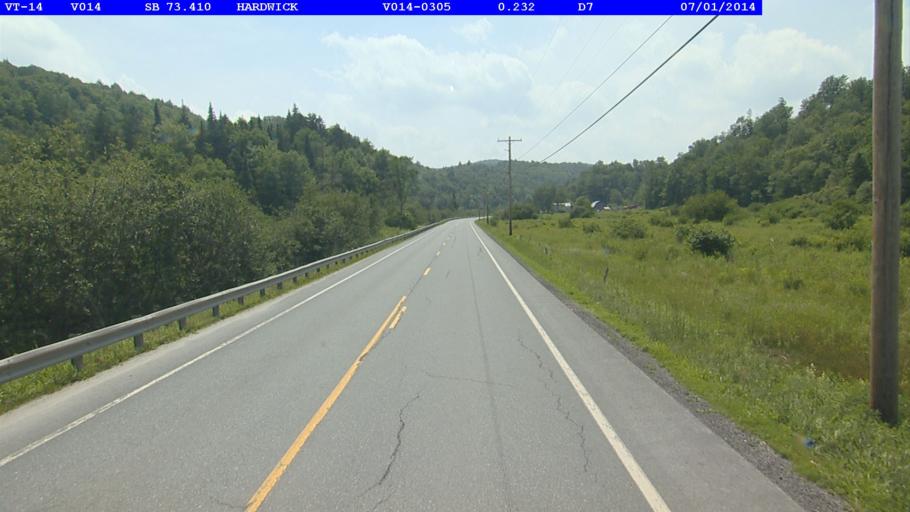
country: US
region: Vermont
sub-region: Caledonia County
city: Hardwick
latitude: 44.4888
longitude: -72.3796
